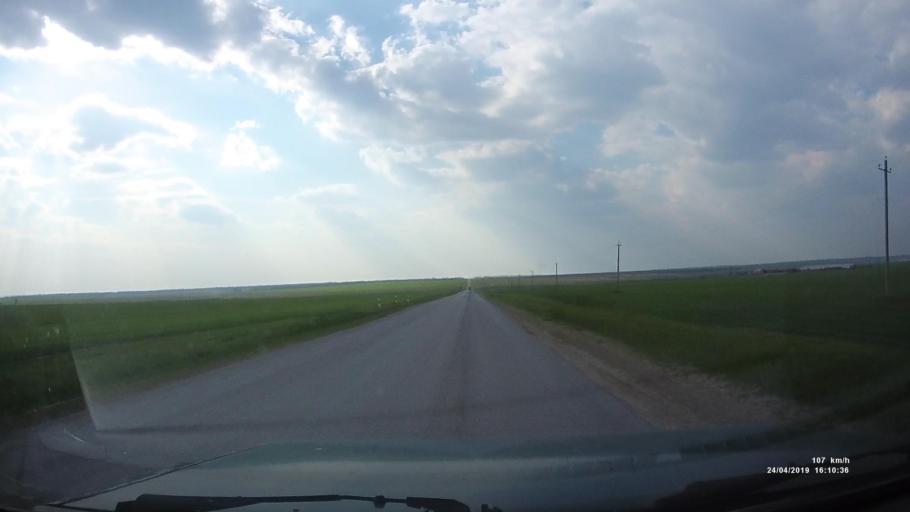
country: RU
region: Rostov
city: Sovetskoye
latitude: 46.7185
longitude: 42.2675
